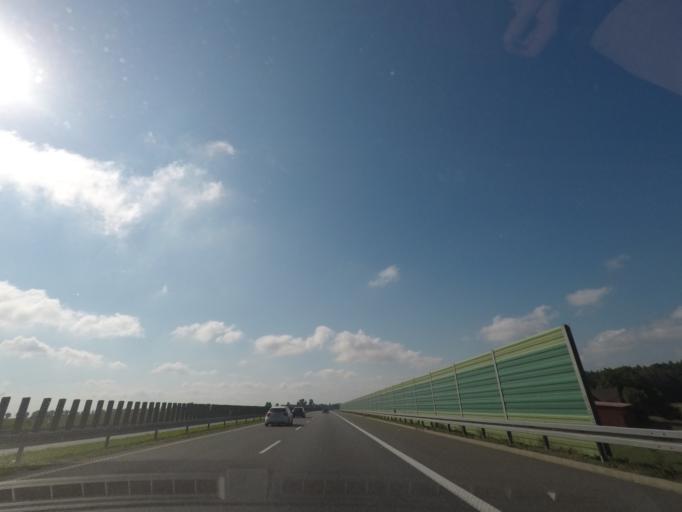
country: PL
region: Pomeranian Voivodeship
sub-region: Powiat tczewski
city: Pelplin
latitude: 53.9200
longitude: 18.6429
